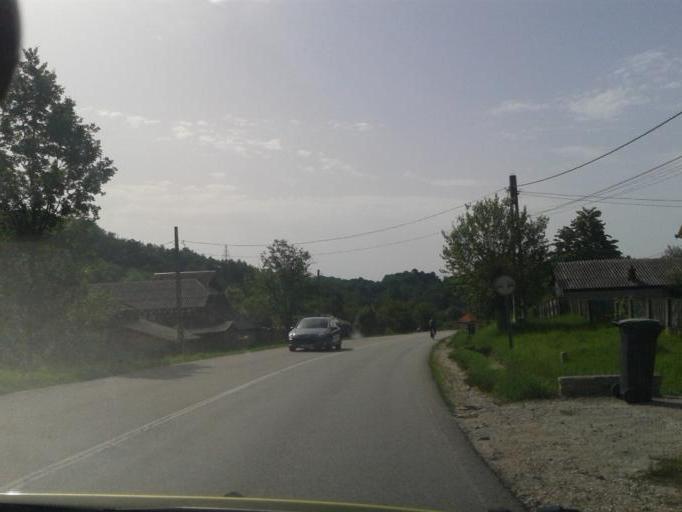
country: RO
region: Valcea
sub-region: Comuna Pietrari
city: Pietrarii de Sus
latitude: 45.1352
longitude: 24.0839
